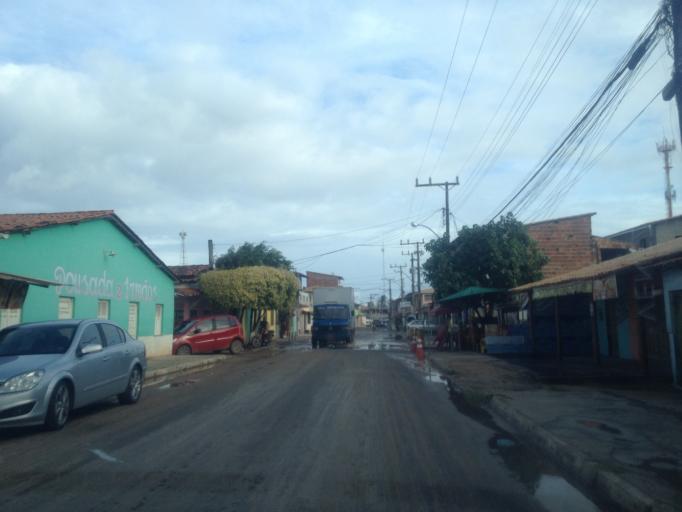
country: BR
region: Bahia
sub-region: Mata De Sao Joao
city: Mata de Sao Joao
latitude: -12.3876
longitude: -37.8823
